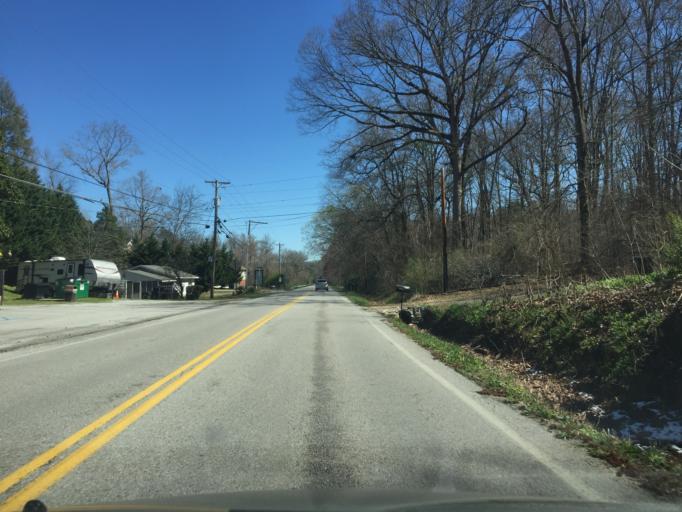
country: US
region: Tennessee
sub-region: Hamilton County
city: Collegedale
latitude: 35.0735
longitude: -85.0933
